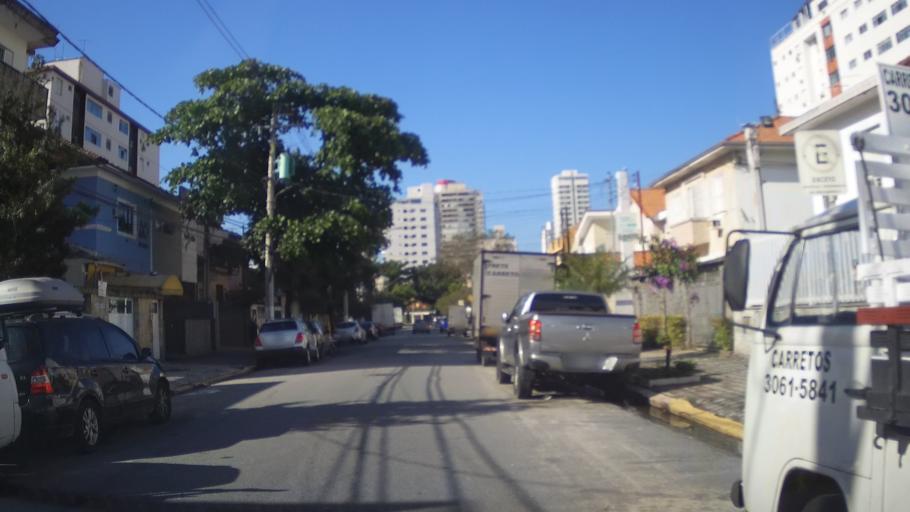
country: BR
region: Sao Paulo
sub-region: Santos
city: Santos
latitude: -23.9583
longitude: -46.3264
